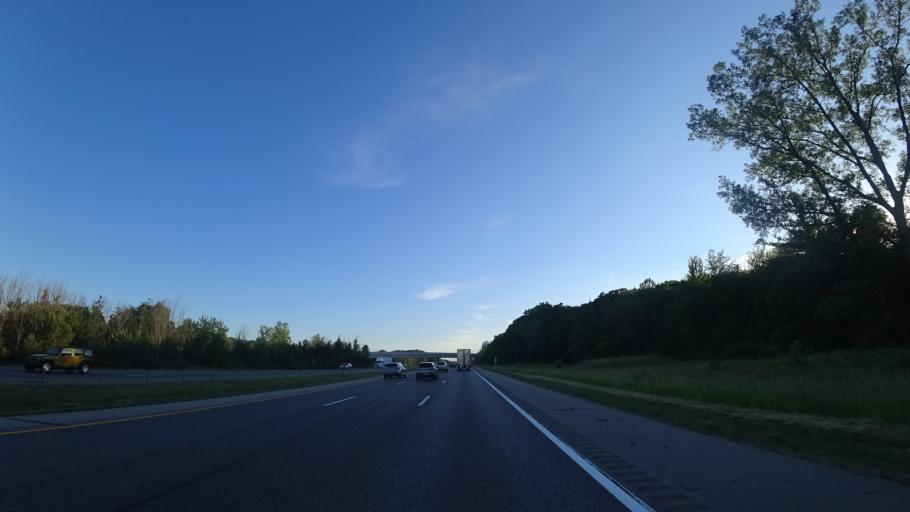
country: US
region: Michigan
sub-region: Berrien County
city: Shorewood-Tower Hills-Harbert
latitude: 41.8409
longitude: -86.6514
